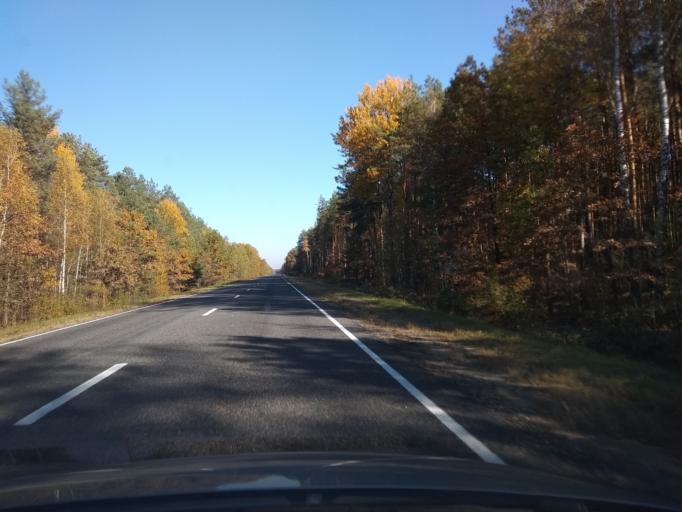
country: BY
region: Brest
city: Malaryta
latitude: 51.9441
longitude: 24.1783
